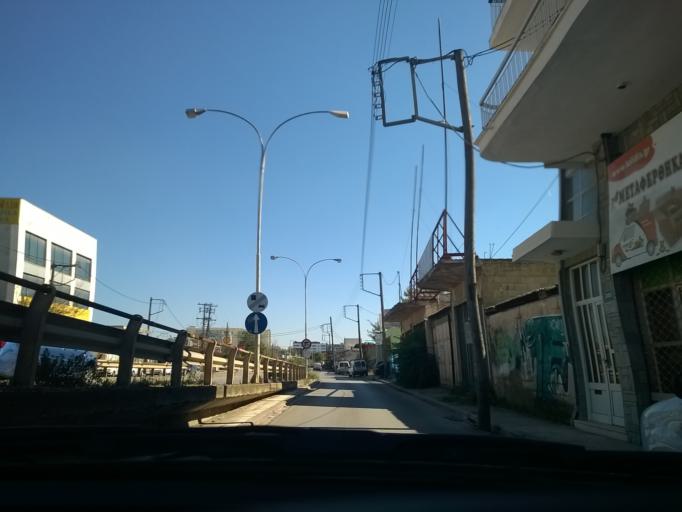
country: GR
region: Central Macedonia
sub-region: Nomos Thessalonikis
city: Menemeni
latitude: 40.6606
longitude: 22.8994
